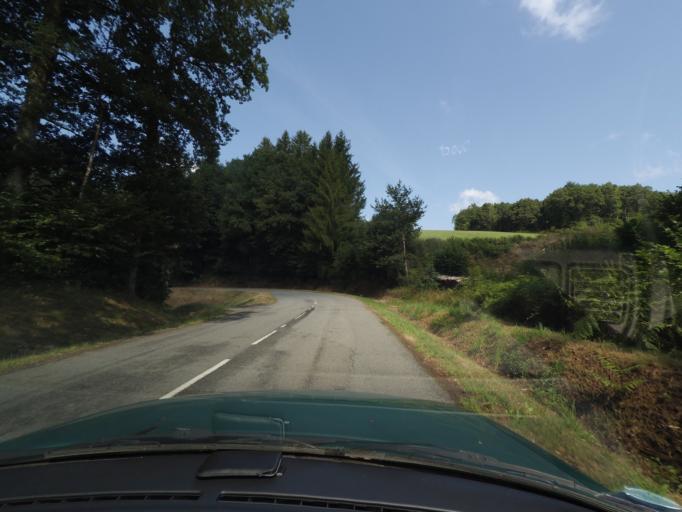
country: FR
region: Limousin
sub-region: Departement de la Haute-Vienne
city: Eymoutiers
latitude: 45.7209
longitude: 1.8248
